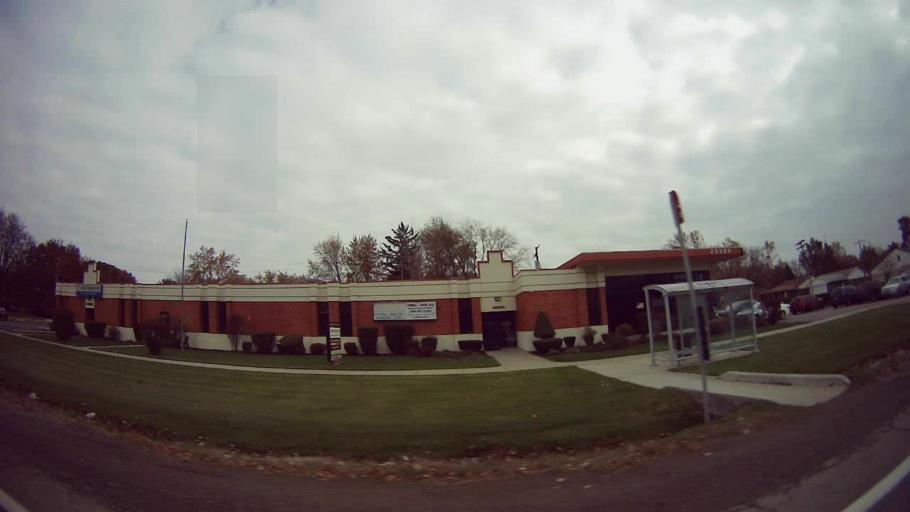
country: US
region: Michigan
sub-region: Oakland County
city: Lathrup Village
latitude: 42.4991
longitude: -83.2224
